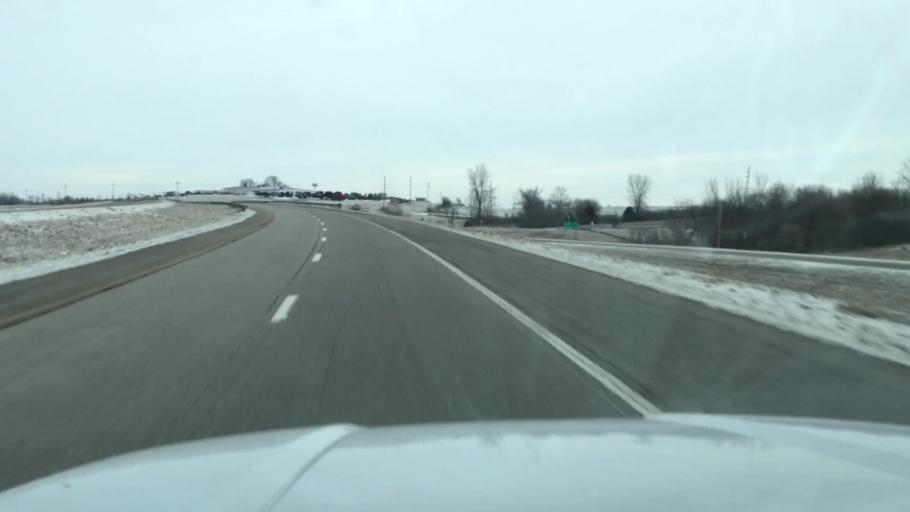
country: US
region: Missouri
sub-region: Andrew County
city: Savannah
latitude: 39.9595
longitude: -94.8602
